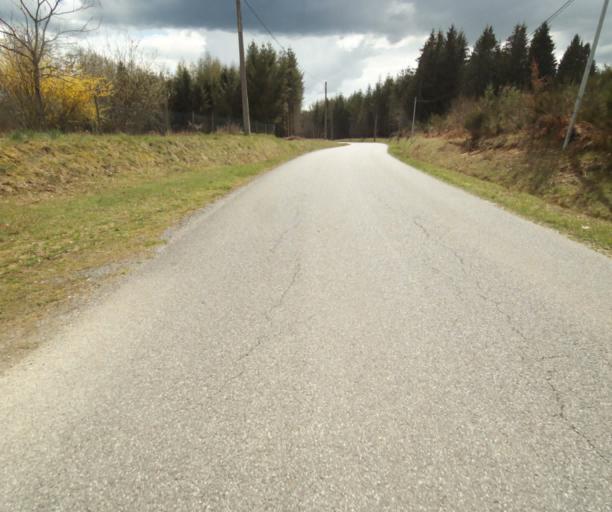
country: FR
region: Limousin
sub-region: Departement de la Correze
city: Correze
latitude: 45.2727
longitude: 1.9696
